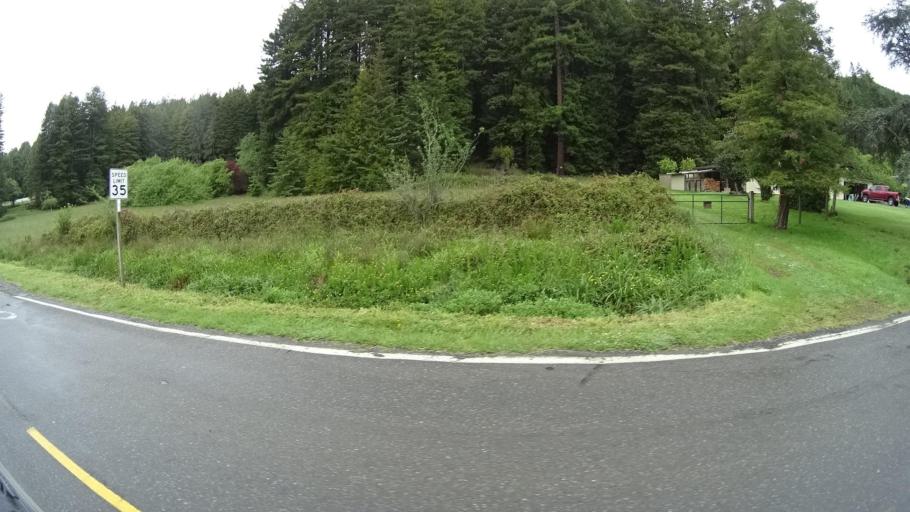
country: US
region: California
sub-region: Humboldt County
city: Bayside
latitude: 40.8328
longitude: -124.0437
